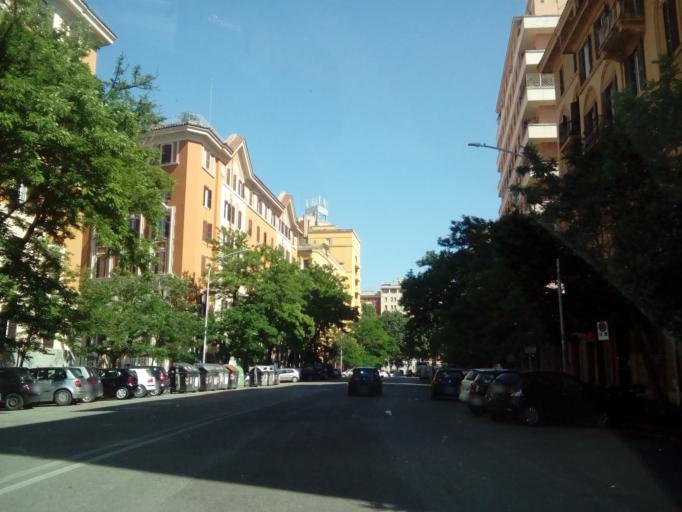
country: IT
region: Latium
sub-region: Citta metropolitana di Roma Capitale
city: Rome
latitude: 41.8830
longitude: 12.5209
